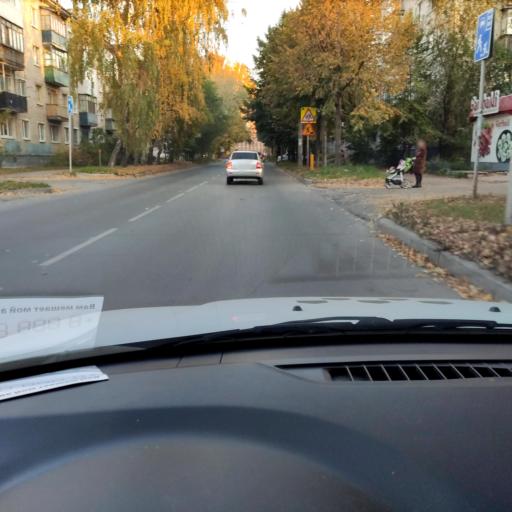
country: RU
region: Samara
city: Tol'yatti
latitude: 53.5105
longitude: 49.4049
